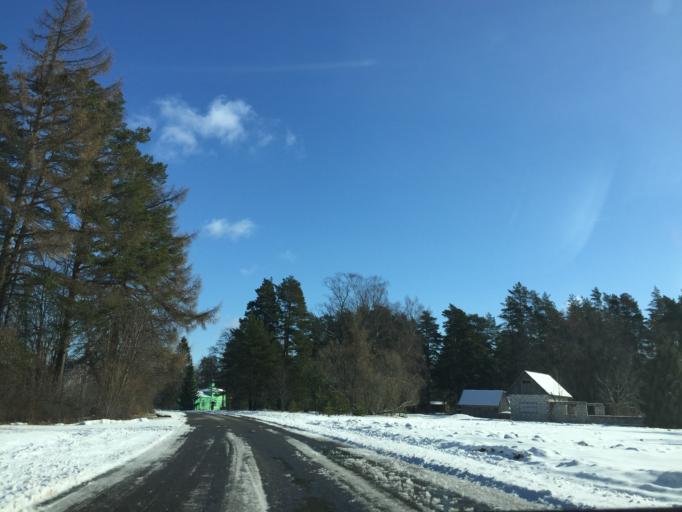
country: LV
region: Aloja
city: Staicele
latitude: 58.0231
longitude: 24.6009
